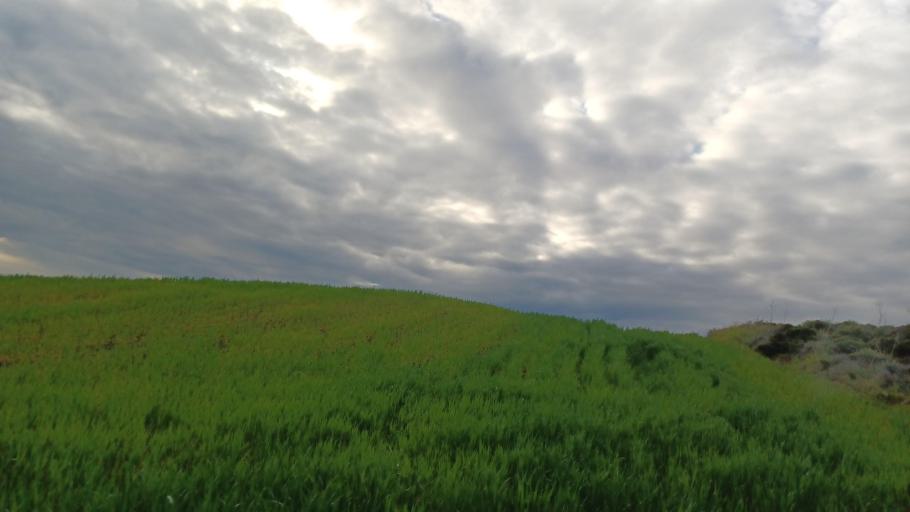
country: CY
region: Lefkosia
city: Lefka
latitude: 35.0792
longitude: 32.8981
